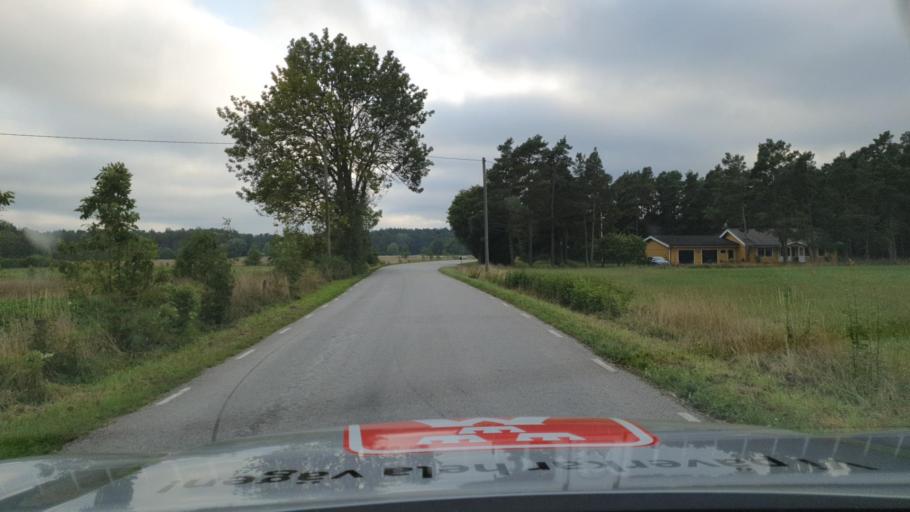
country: SE
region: Gotland
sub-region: Gotland
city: Vibble
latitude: 57.5019
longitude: 18.2004
